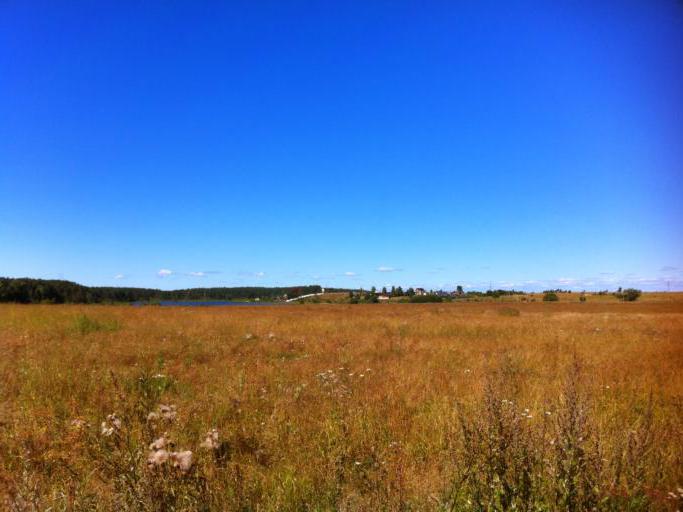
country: RU
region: Pskov
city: Izborsk
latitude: 57.8191
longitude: 27.9596
